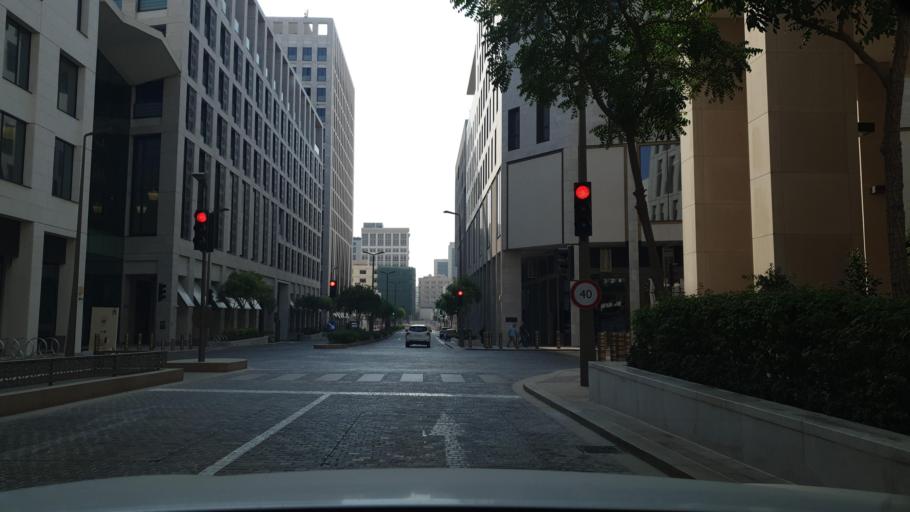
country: QA
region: Baladiyat ad Dawhah
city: Doha
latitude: 25.2860
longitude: 51.5276
